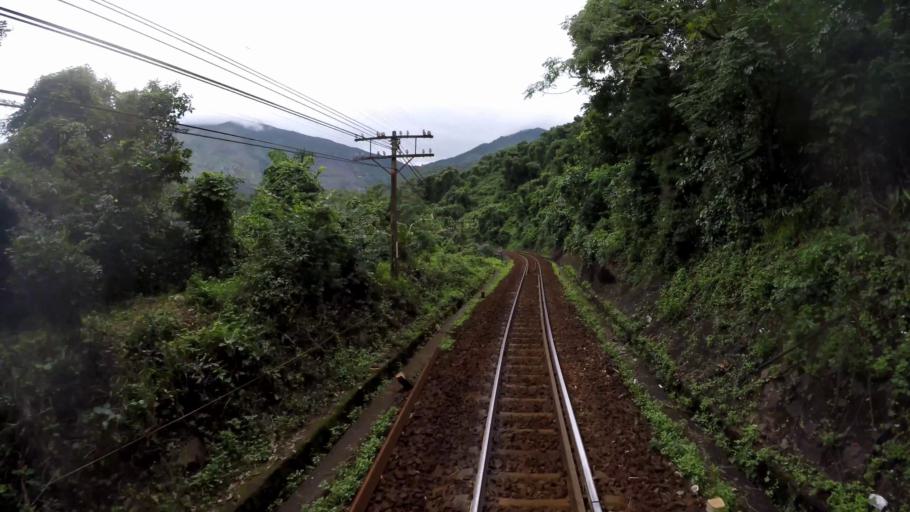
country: VN
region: Da Nang
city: Lien Chieu
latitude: 16.1711
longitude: 108.1460
